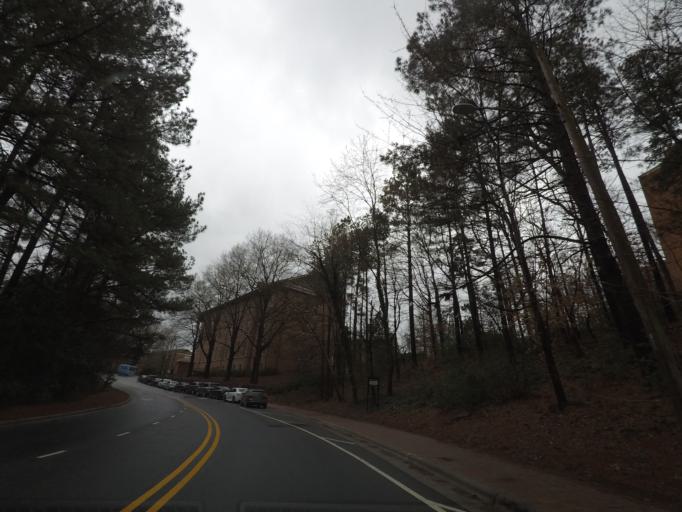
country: US
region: North Carolina
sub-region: Orange County
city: Chapel Hill
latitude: 35.9053
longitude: -79.0454
